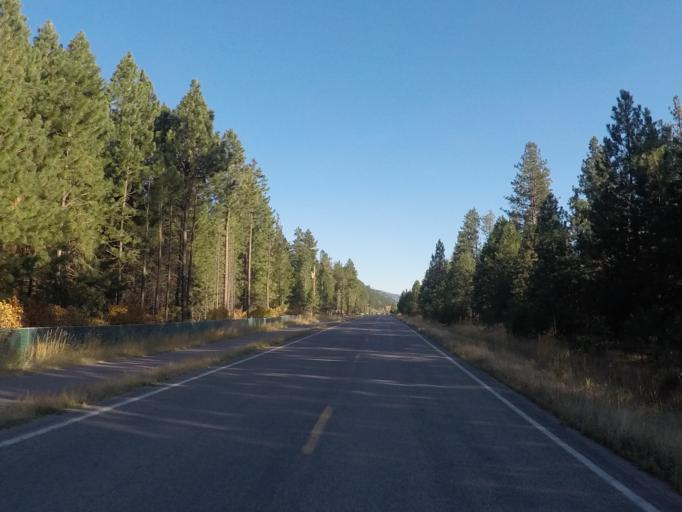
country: US
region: Montana
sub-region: Missoula County
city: Bonner-West Riverside
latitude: 46.8403
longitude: -113.8342
